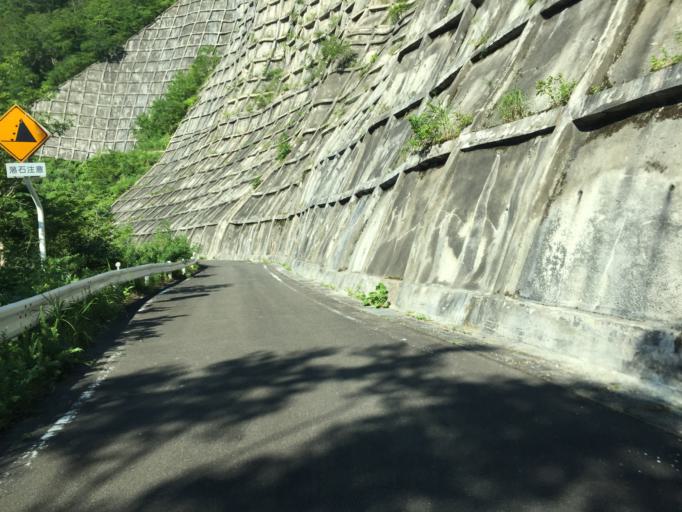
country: JP
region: Yamagata
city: Takahata
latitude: 37.9502
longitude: 140.3438
